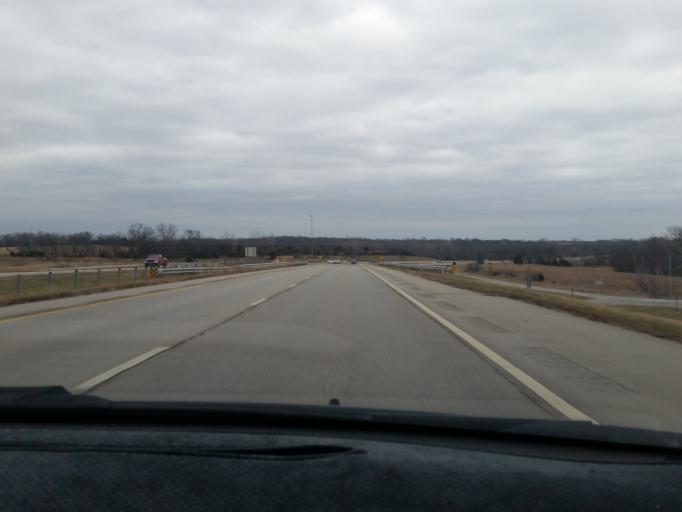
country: US
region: Kansas
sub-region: Douglas County
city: Eudora
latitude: 38.9402
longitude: -95.0742
